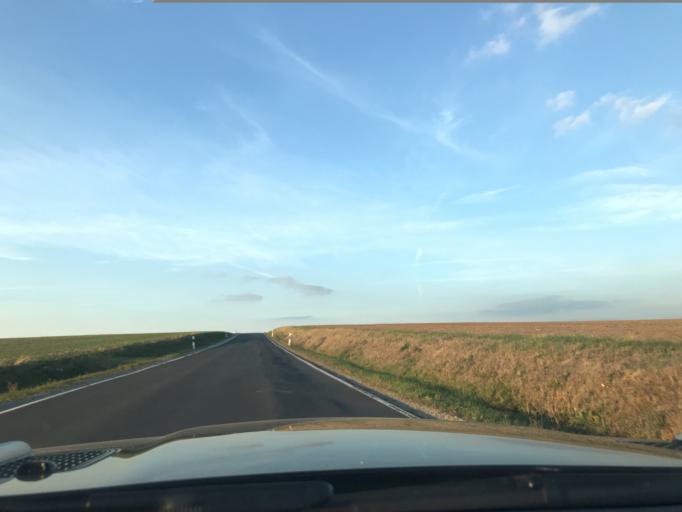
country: DE
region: Thuringia
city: Oppershausen
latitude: 51.1458
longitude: 10.4420
